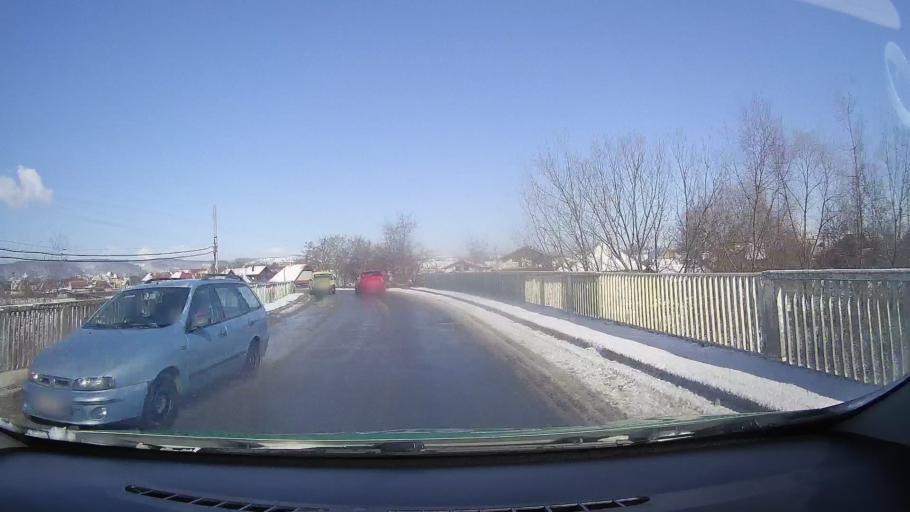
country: RO
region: Sibiu
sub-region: Comuna Avrig
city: Avrig
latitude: 45.7192
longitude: 24.3740
